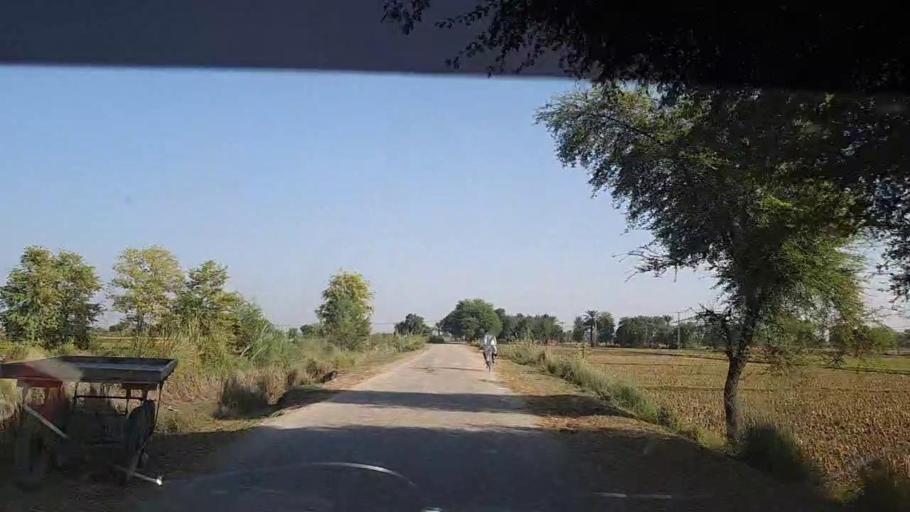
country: PK
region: Sindh
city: Larkana
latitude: 27.6229
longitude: 68.2425
